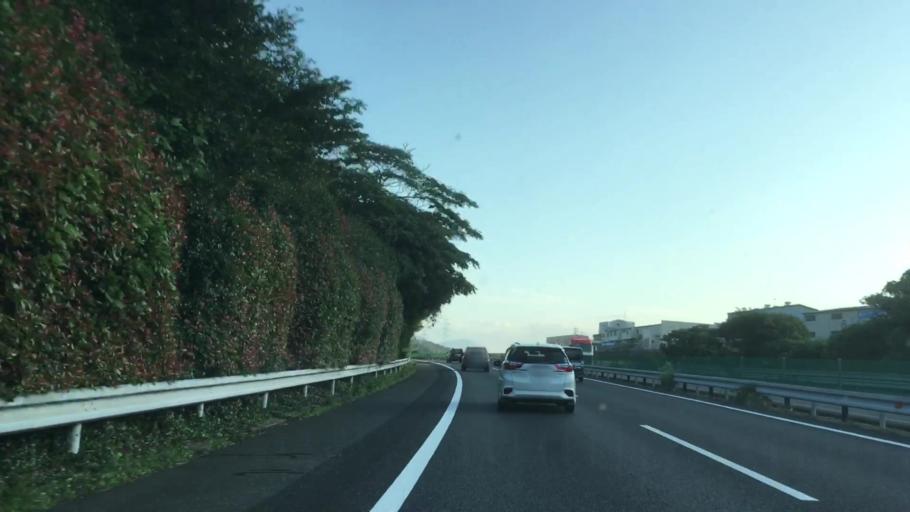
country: JP
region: Yamaguchi
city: Shimonoseki
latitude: 33.9871
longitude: 130.9512
